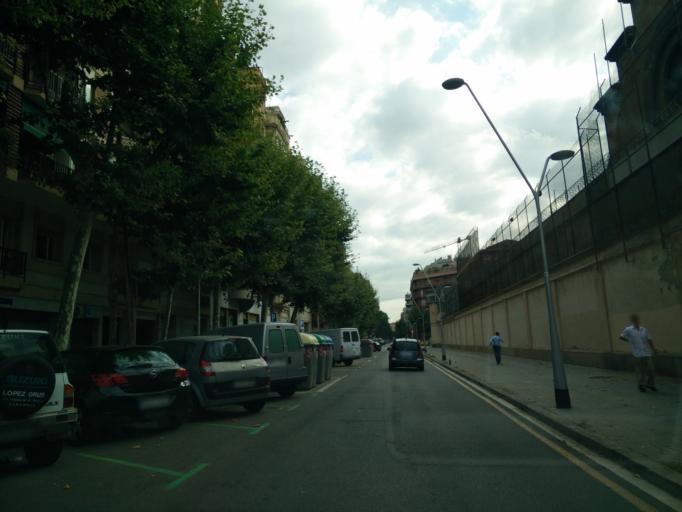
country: ES
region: Catalonia
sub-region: Provincia de Barcelona
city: les Corts
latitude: 41.3830
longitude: 2.1436
